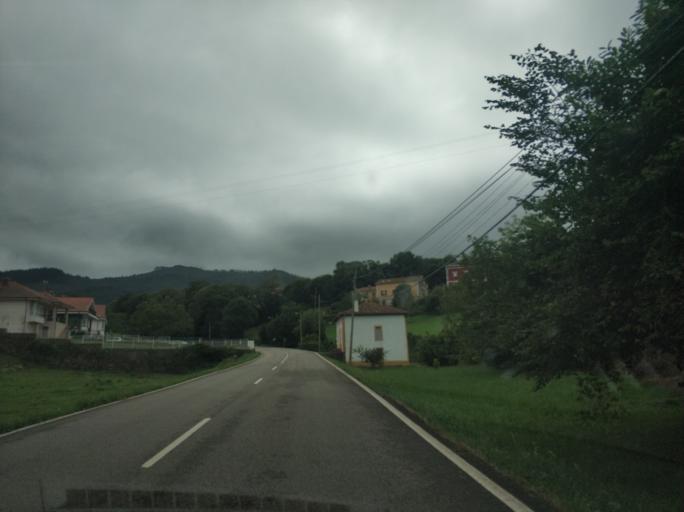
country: ES
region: Asturias
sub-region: Province of Asturias
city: Cudillero
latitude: 43.5477
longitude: -6.2217
